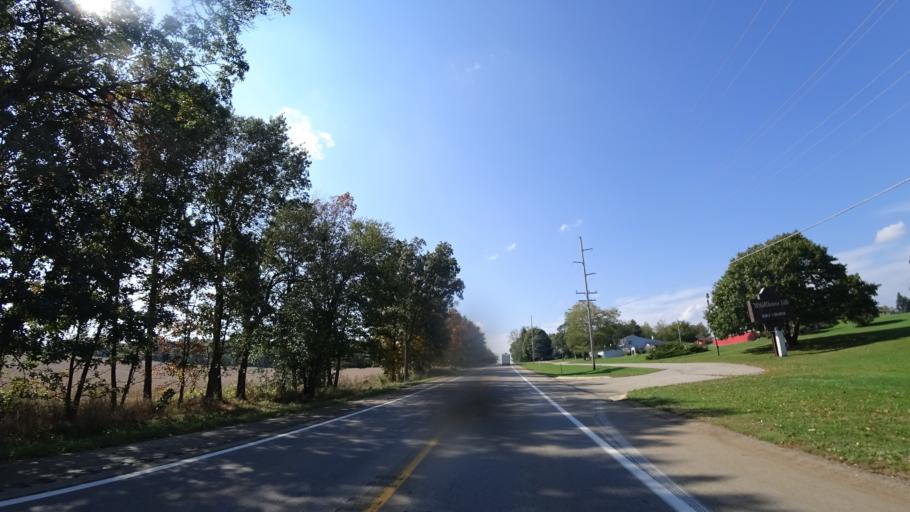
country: US
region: Michigan
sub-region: Jackson County
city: Concord
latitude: 42.1633
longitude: -84.7045
